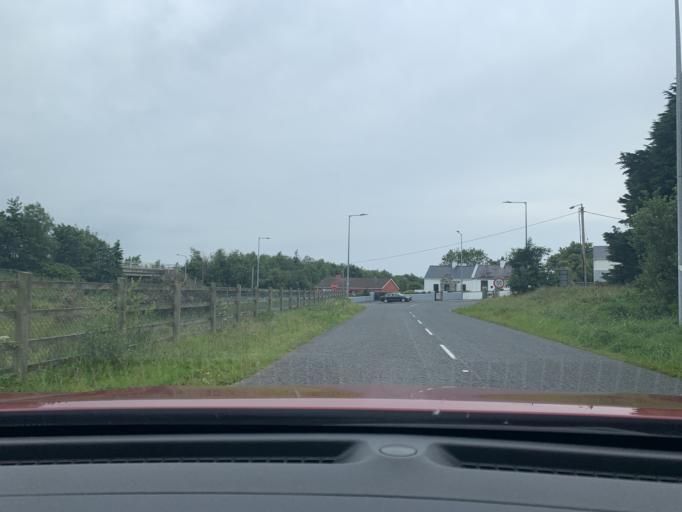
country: IE
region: Ulster
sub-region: County Donegal
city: Bundoran
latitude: 54.4717
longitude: -8.2748
